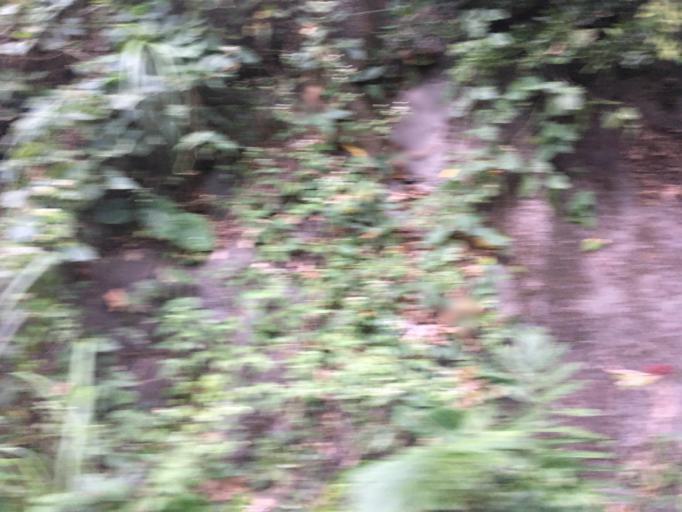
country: TW
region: Taiwan
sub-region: Chiayi
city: Jiayi Shi
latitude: 23.5348
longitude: 120.6037
